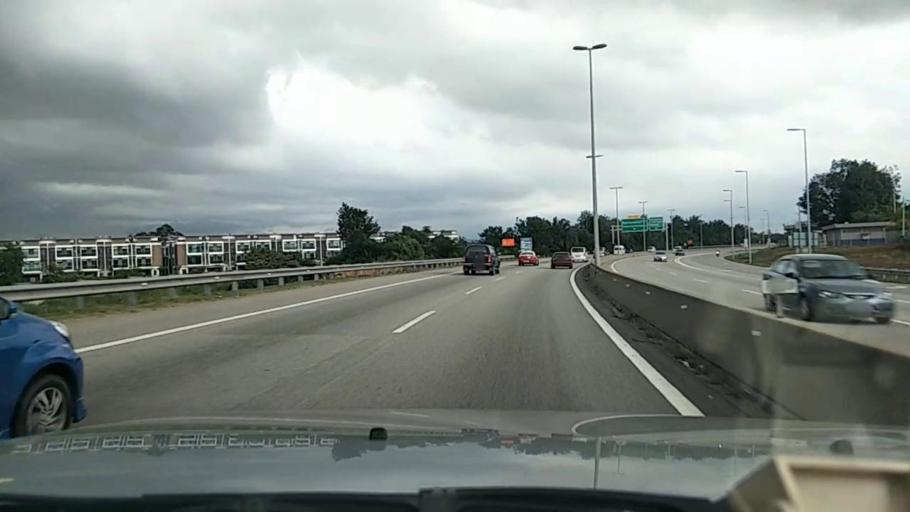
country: MY
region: Putrajaya
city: Putrajaya
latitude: 2.9376
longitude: 101.6263
